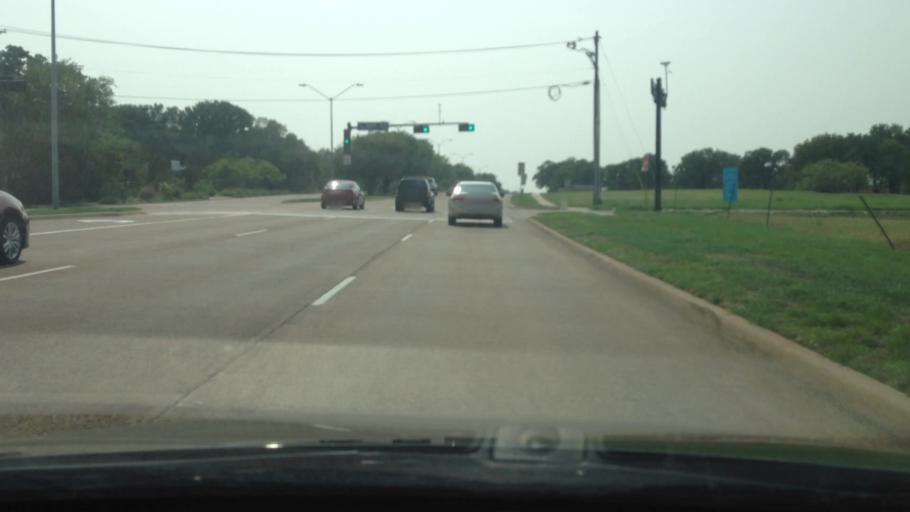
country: US
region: Texas
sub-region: Tarrant County
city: Colleyville
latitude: 32.8619
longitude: -97.1942
